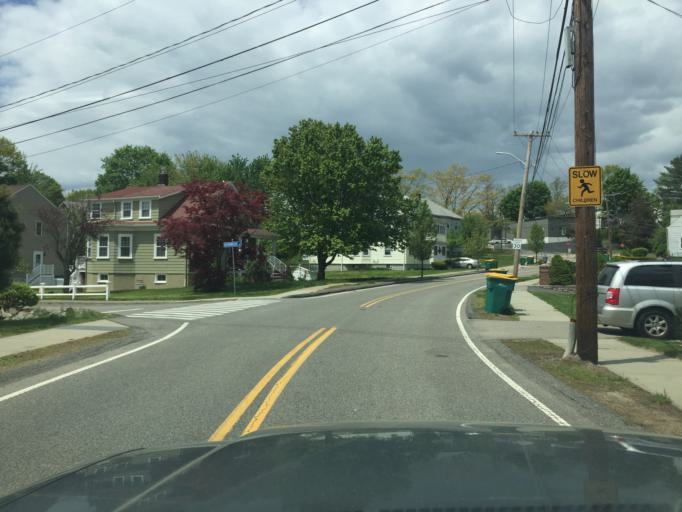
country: US
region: Massachusetts
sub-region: Norfolk County
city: Norwood
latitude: 42.1828
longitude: -71.1989
